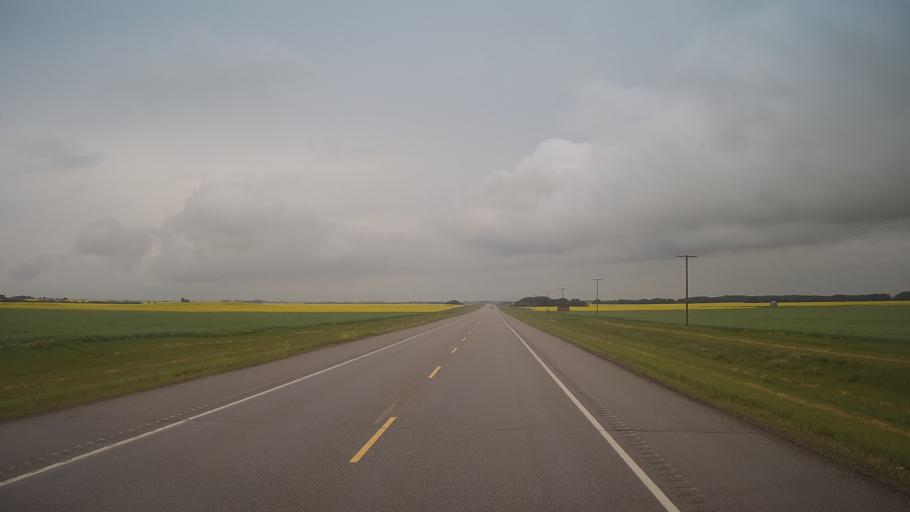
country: CA
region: Saskatchewan
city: Wilkie
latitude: 52.4228
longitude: -108.9010
